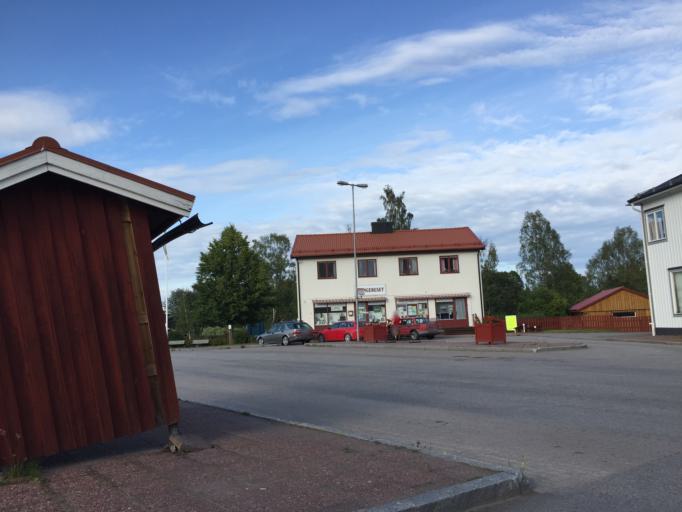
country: SE
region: Dalarna
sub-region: Ludvika Kommun
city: Grangesberg
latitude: 60.2620
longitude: 14.9774
